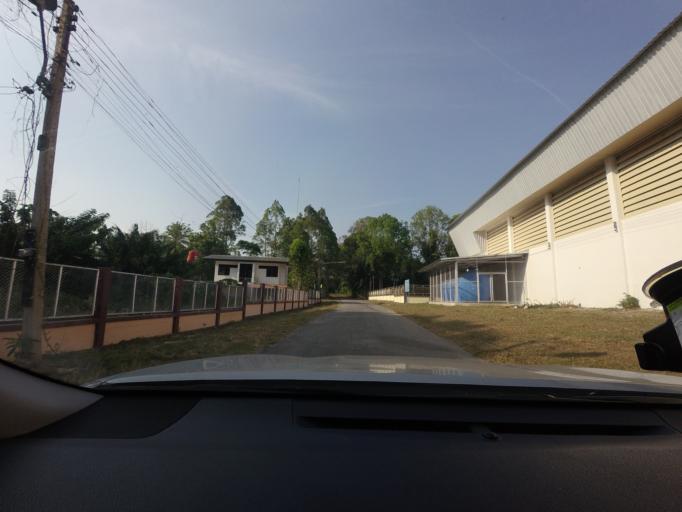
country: TH
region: Narathiwat
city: Rueso
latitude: 6.3998
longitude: 101.5253
